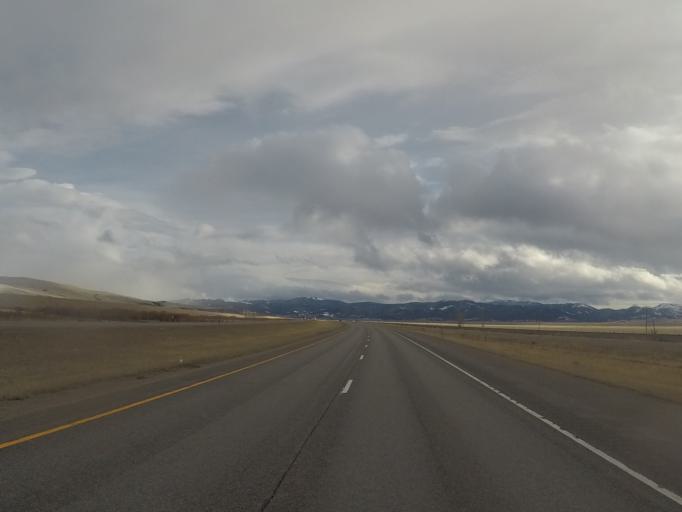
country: US
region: Montana
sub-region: Deer Lodge County
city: Warm Springs
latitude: 46.1665
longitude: -112.7902
